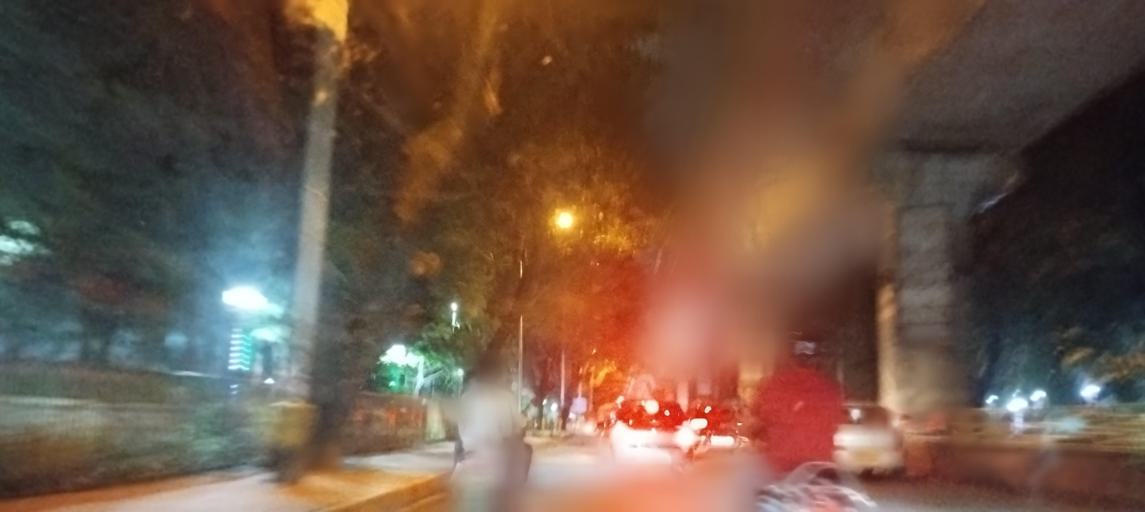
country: IN
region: Karnataka
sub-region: Bangalore Urban
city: Bangalore
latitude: 12.9349
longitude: 77.5800
